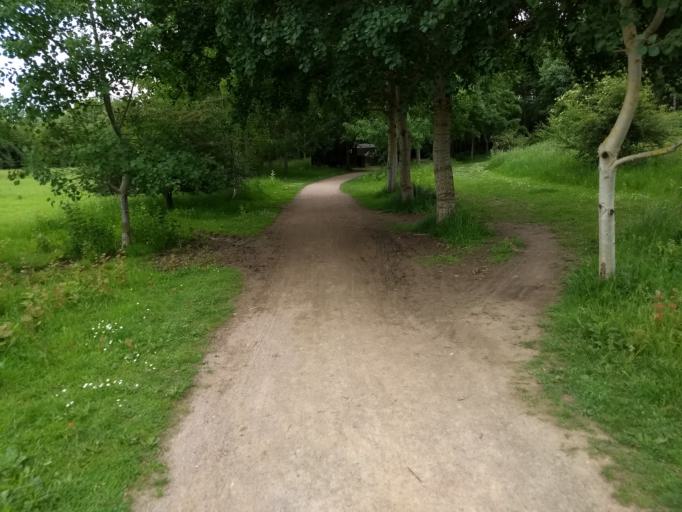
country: GB
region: England
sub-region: Central Bedfordshire
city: Marston Moretaine
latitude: 52.0658
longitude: -0.5365
